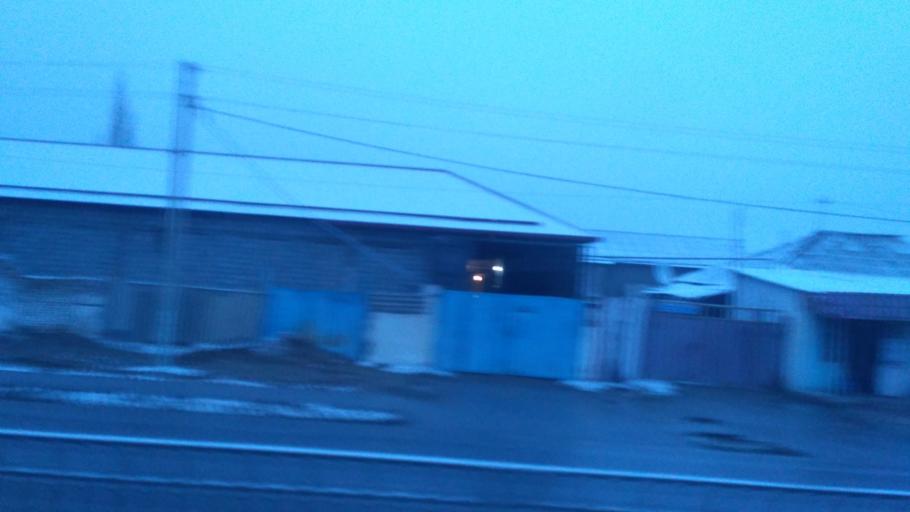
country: KZ
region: Ongtustik Qazaqstan
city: Shymkent
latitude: 42.3758
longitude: 69.4998
